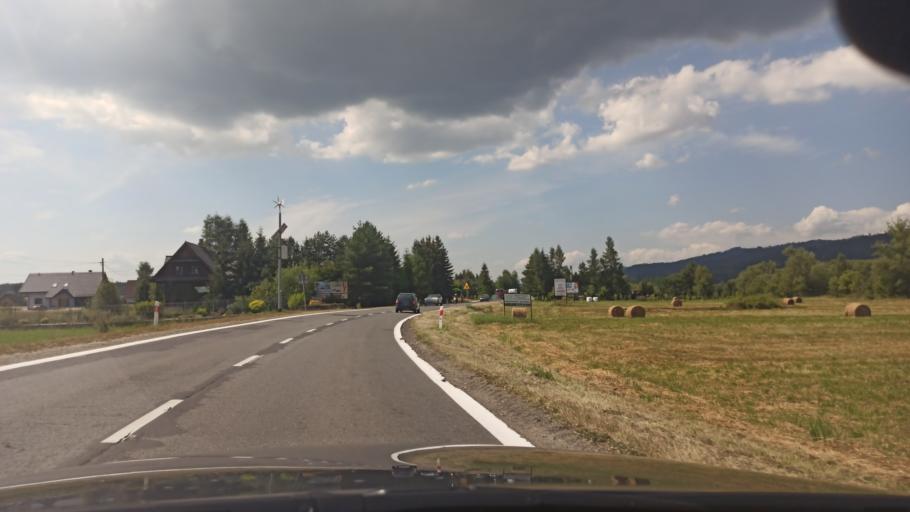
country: PL
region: Lesser Poland Voivodeship
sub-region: Powiat nowotarski
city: Lopuszna
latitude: 49.4689
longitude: 20.1387
